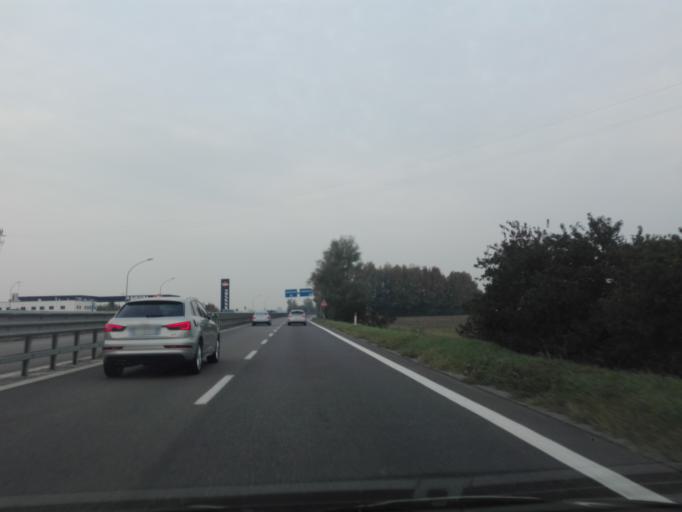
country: IT
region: Veneto
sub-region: Provincia di Rovigo
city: San Bellino
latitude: 45.0268
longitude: 11.5794
